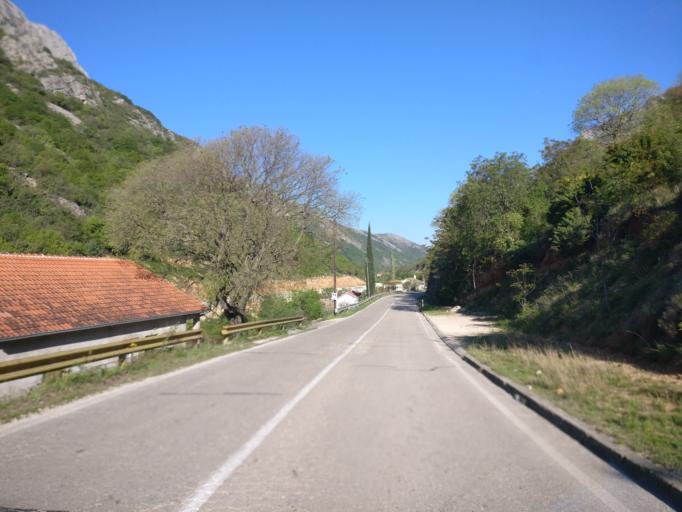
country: BA
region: Federation of Bosnia and Herzegovina
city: Stolac
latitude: 43.0740
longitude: 18.0307
